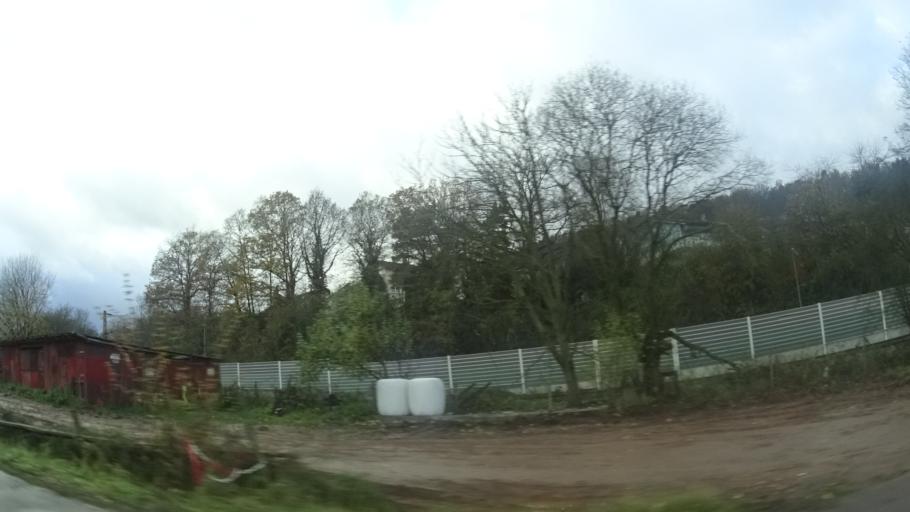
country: DE
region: Hesse
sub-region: Regierungsbezirk Kassel
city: Petersberg
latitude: 50.5851
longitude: 9.7308
